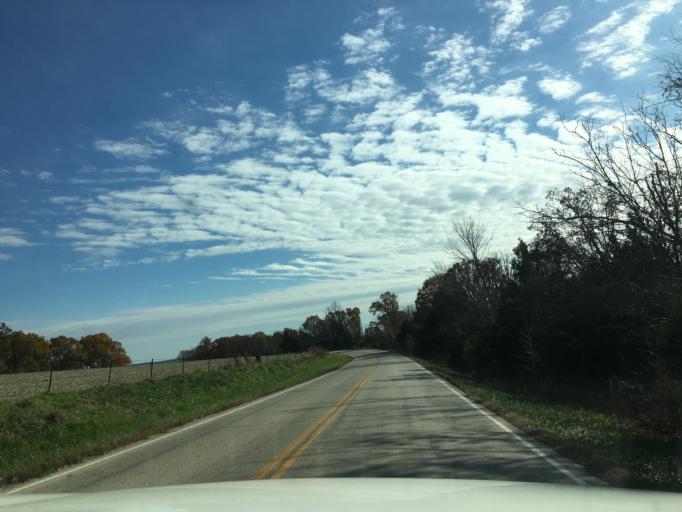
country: US
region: Missouri
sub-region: Osage County
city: Linn
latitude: 38.4163
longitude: -91.8199
